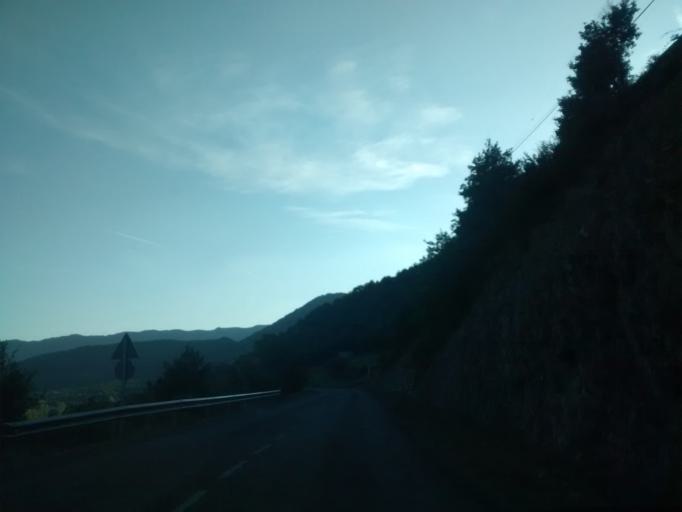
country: ES
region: Aragon
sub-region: Provincia de Huesca
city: Anso
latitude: 42.7640
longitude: -0.7457
